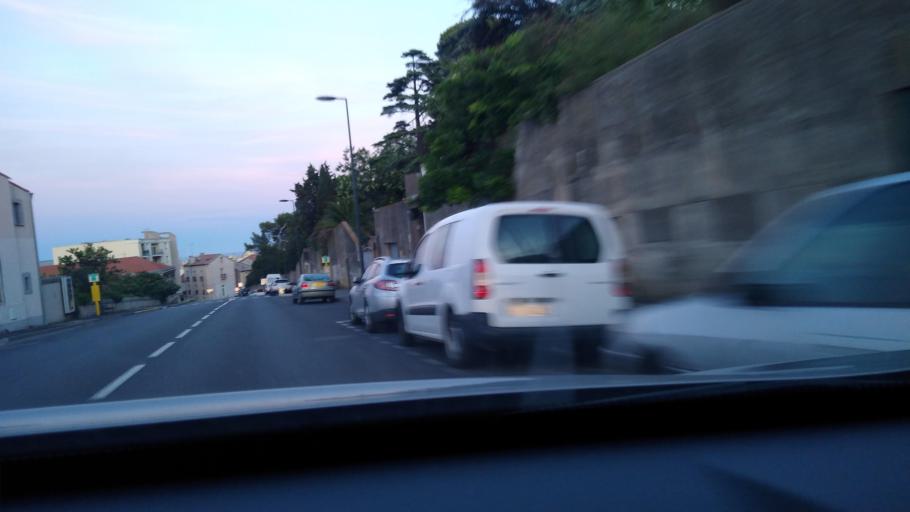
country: FR
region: Languedoc-Roussillon
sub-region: Departement de l'Herault
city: Sete
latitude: 43.4064
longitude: 3.6862
